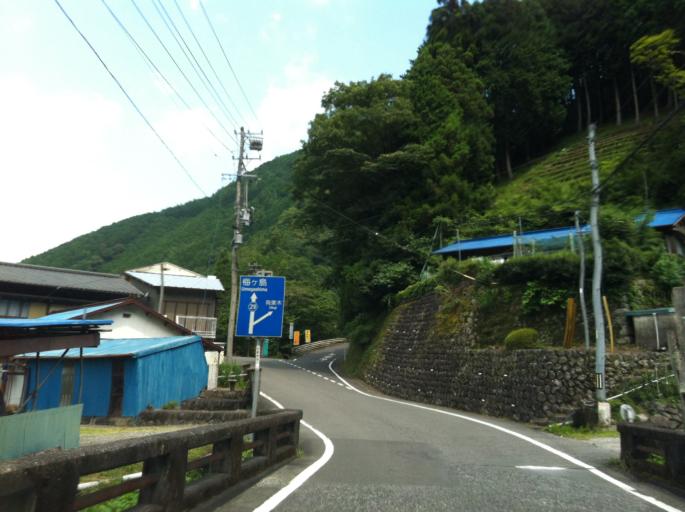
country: JP
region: Shizuoka
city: Shizuoka-shi
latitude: 35.1951
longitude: 138.3625
